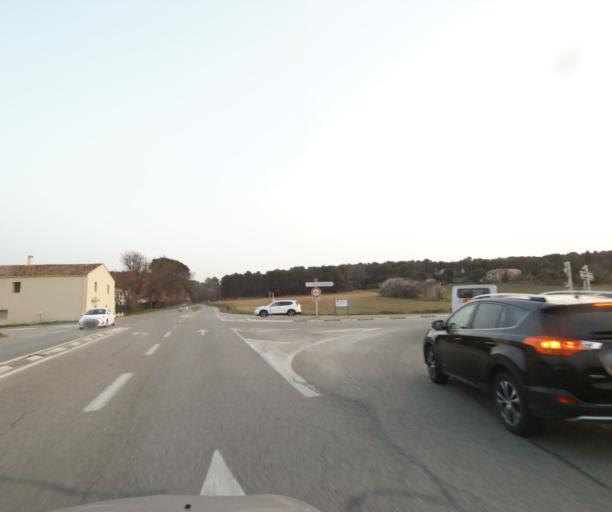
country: FR
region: Provence-Alpes-Cote d'Azur
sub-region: Departement des Bouches-du-Rhone
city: Cabries
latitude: 43.4403
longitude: 5.3615
